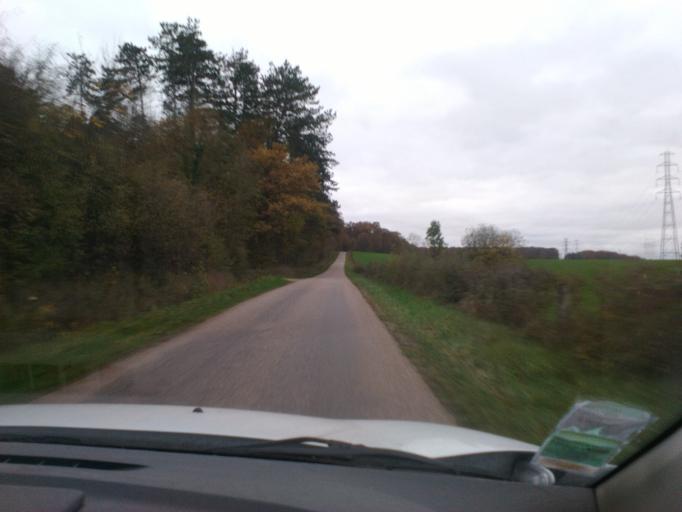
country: FR
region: Lorraine
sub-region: Departement des Vosges
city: Mirecourt
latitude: 48.3014
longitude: 6.2147
